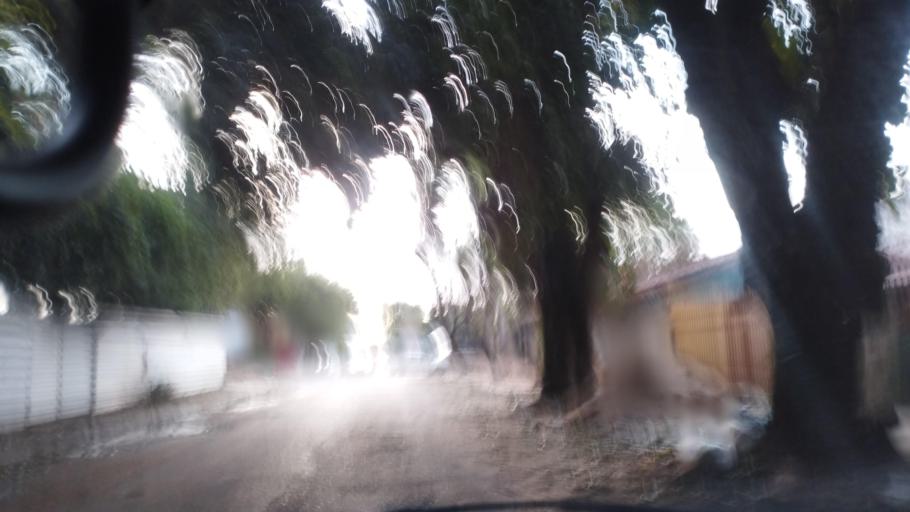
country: PY
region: Central
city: Fernando de la Mora
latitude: -25.3124
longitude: -57.5393
